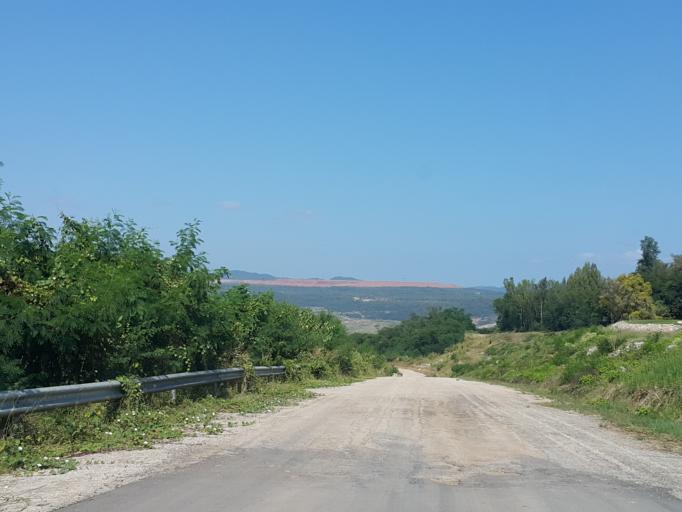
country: TH
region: Lampang
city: Mae Mo
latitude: 18.3204
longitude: 99.7419
